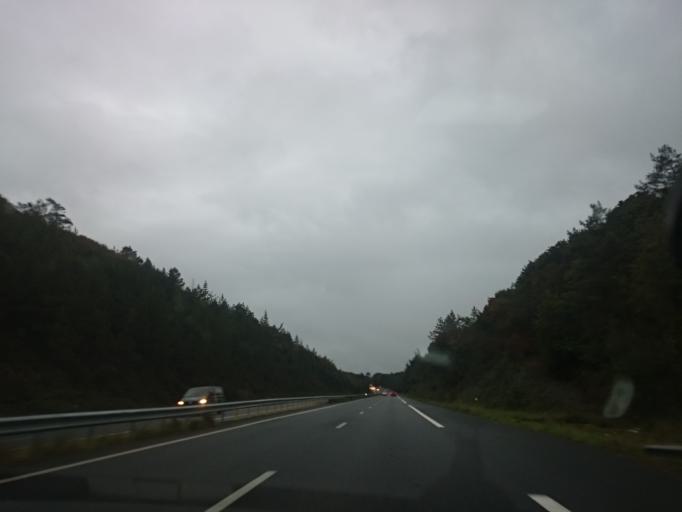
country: FR
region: Brittany
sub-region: Departement du Finistere
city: Hopital-Camfrout
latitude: 48.3388
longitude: -4.2300
